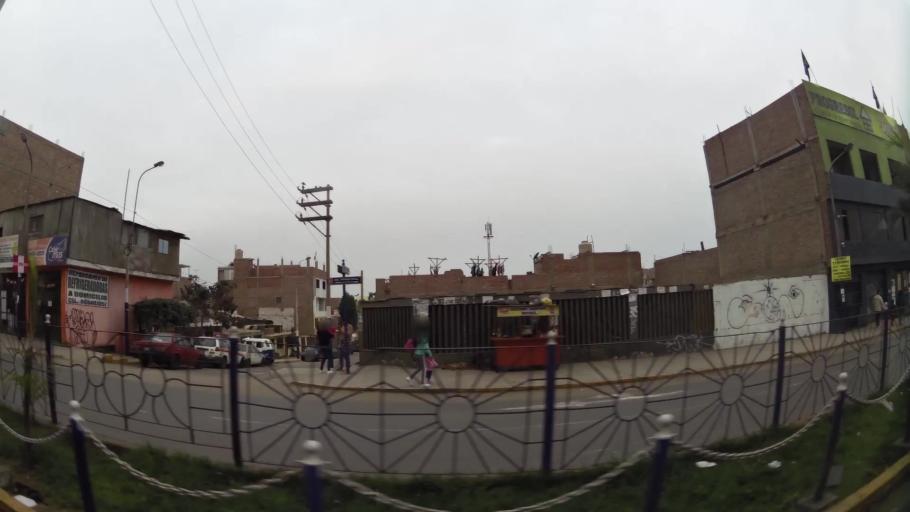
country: PE
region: Lima
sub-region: Lima
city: Surco
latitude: -12.1933
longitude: -77.0199
